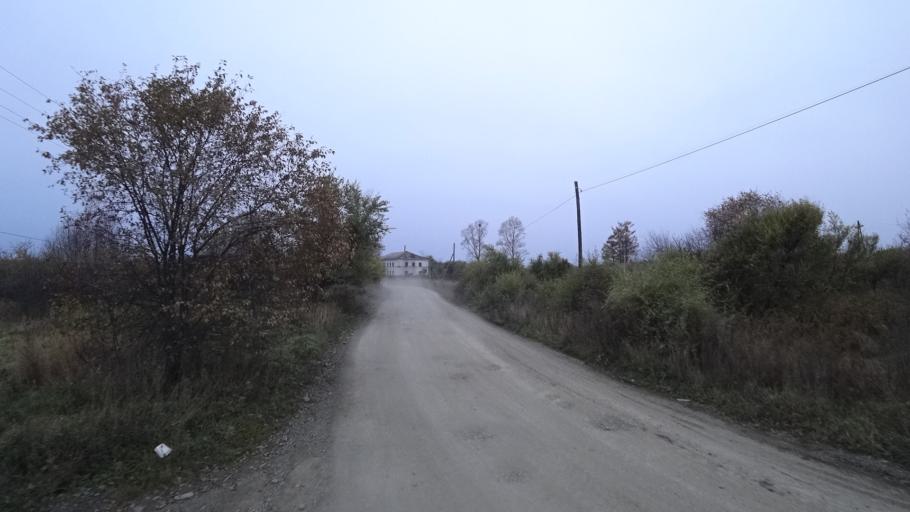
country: RU
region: Khabarovsk Krai
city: Amursk
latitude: 49.9030
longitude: 136.1439
